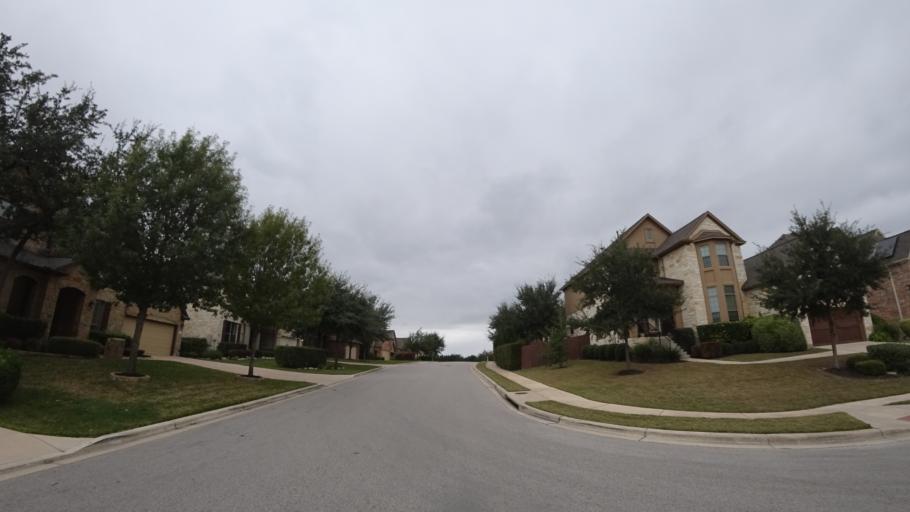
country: US
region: Texas
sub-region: Travis County
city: Bee Cave
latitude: 30.3420
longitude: -97.9100
